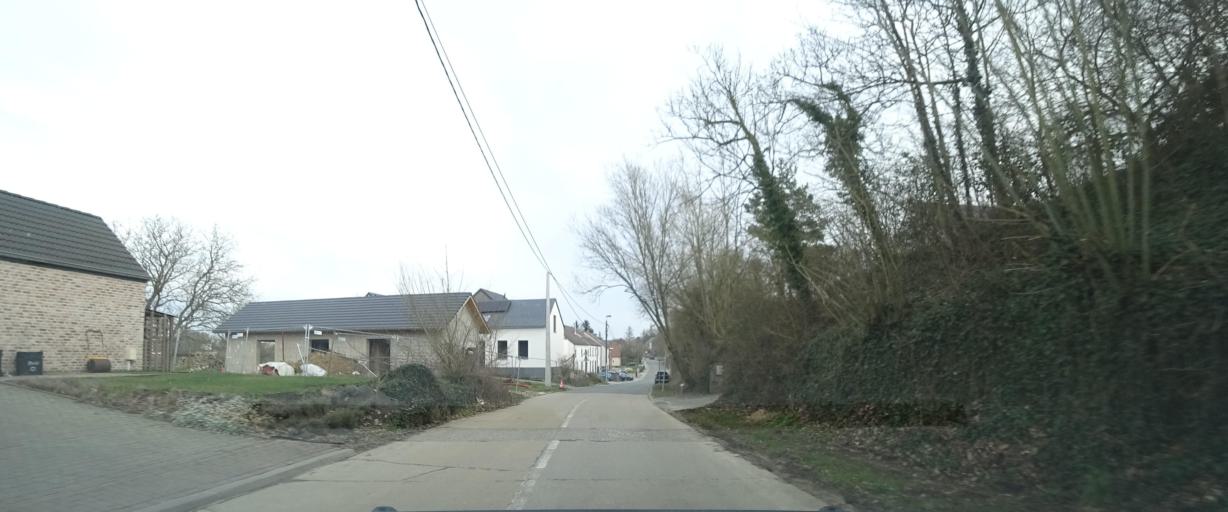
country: BE
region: Wallonia
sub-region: Province du Brabant Wallon
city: Mont-Saint-Guibert
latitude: 50.6177
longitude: 4.6139
